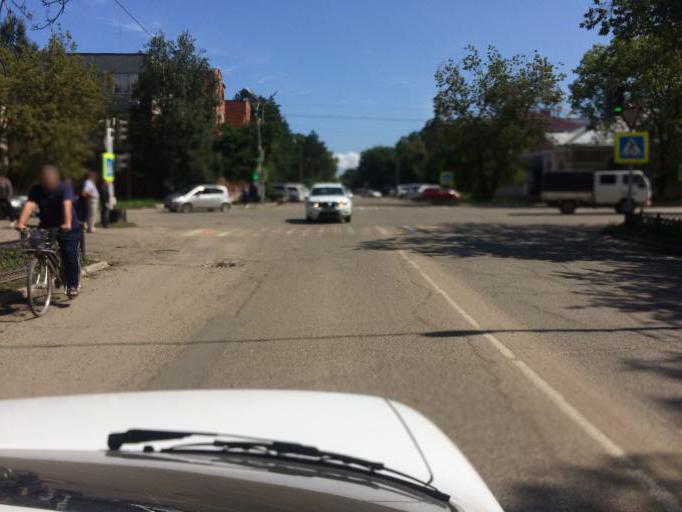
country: RU
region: Primorskiy
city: Dal'nerechensk
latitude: 45.9336
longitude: 133.7346
